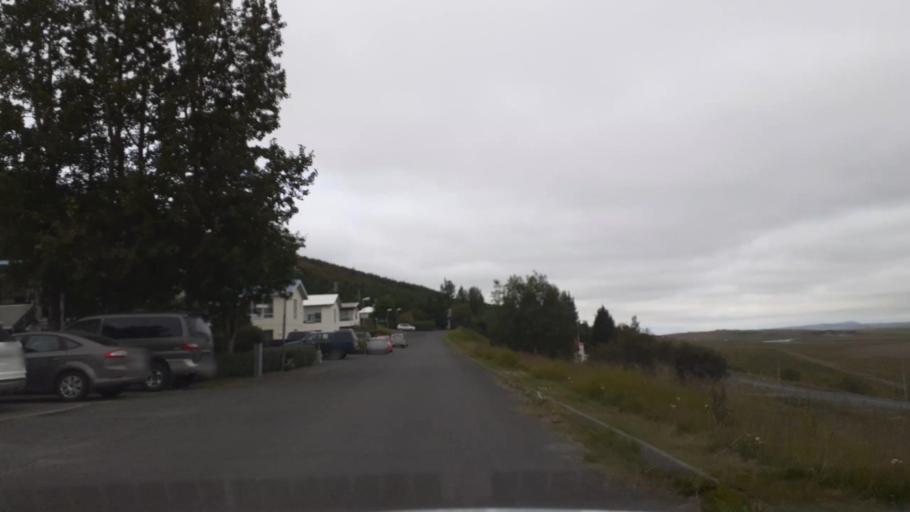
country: IS
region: Northwest
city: Saudarkrokur
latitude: 65.5541
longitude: -19.4489
